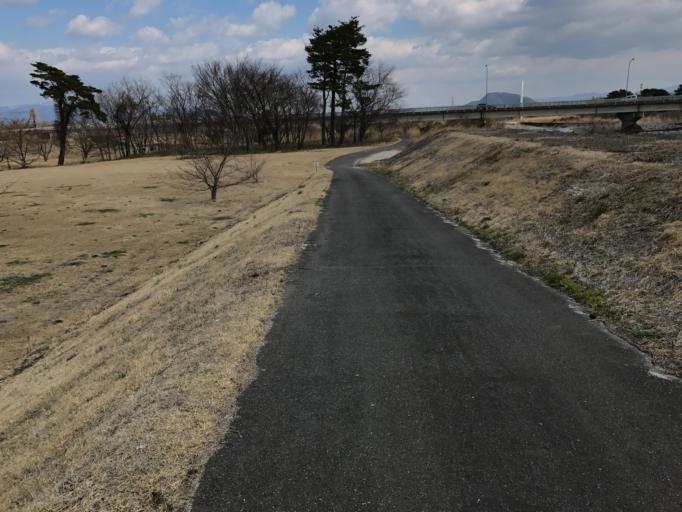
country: JP
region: Fukushima
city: Fukushima-shi
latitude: 37.7459
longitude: 140.4020
